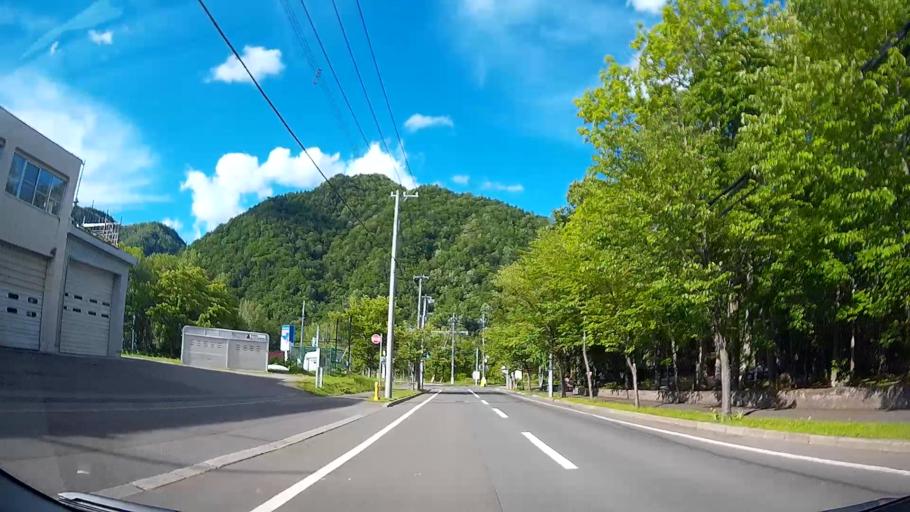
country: JP
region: Hokkaido
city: Sapporo
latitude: 42.9722
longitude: 141.1654
